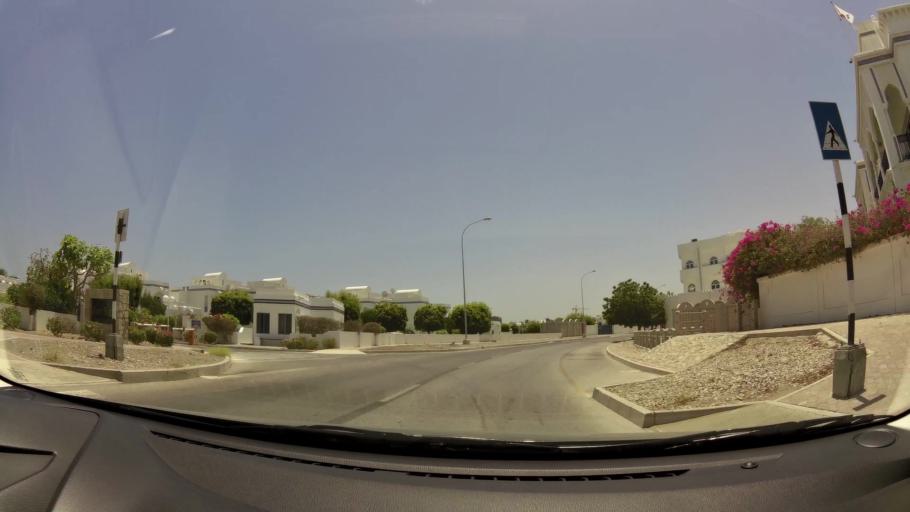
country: OM
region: Muhafazat Masqat
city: Bawshar
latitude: 23.6140
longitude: 58.4594
